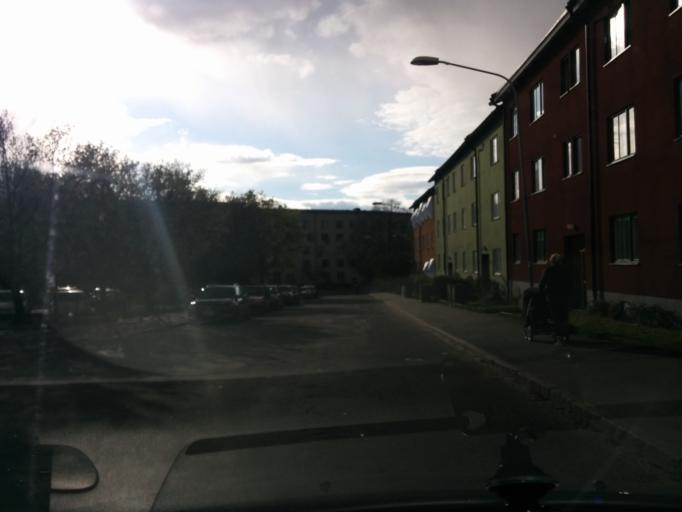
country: SE
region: Stockholm
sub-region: Solna Kommun
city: Solna
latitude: 59.3061
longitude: 17.9902
